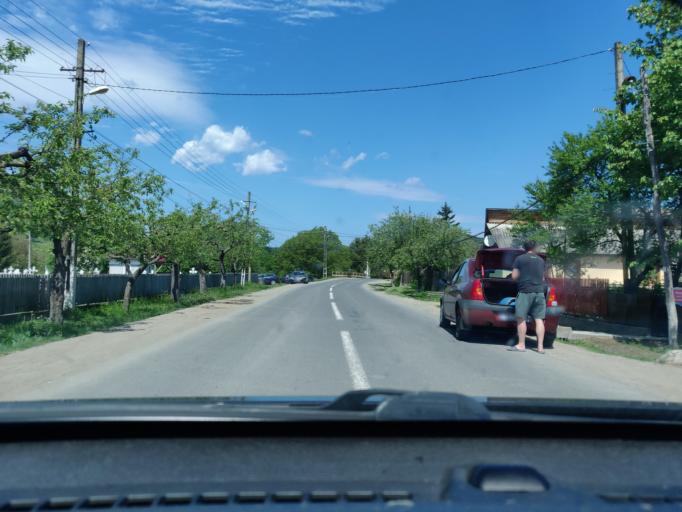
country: RO
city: Campurile de Jos
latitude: 46.0282
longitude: 26.7611
